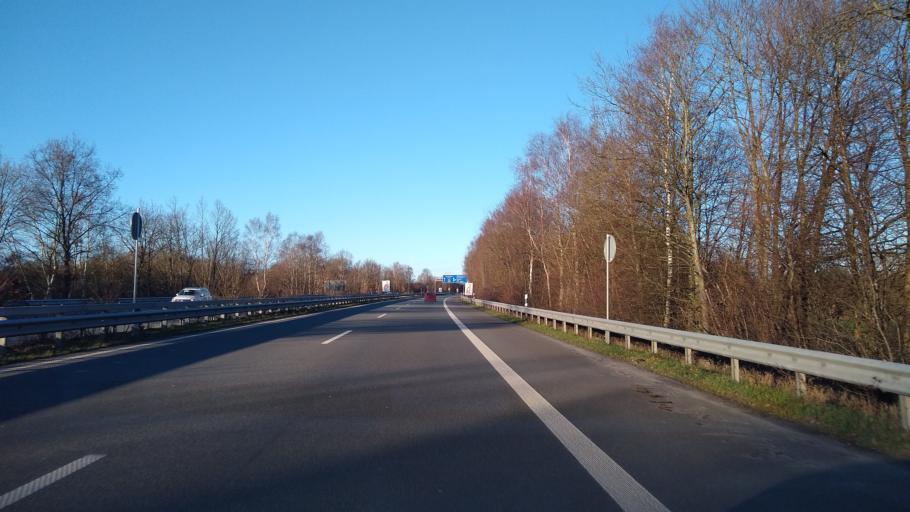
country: DE
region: Lower Saxony
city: Rastede
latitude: 53.1977
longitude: 8.2216
